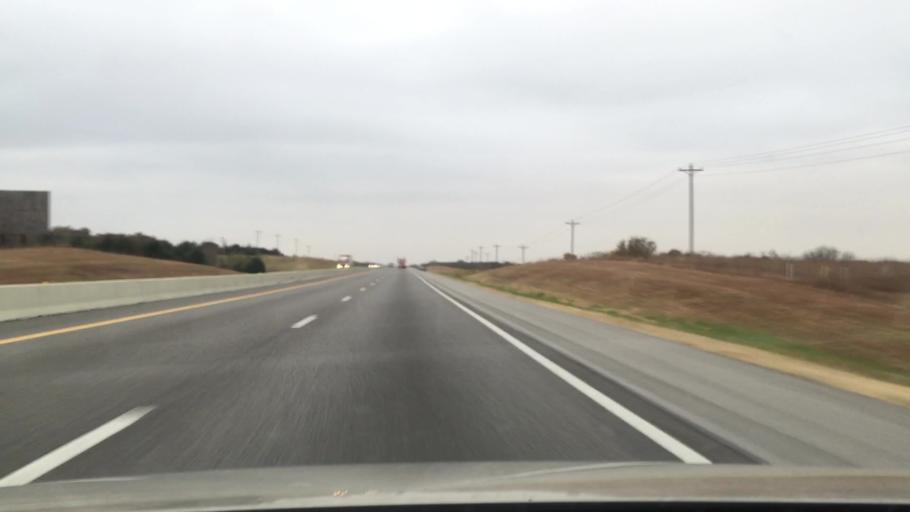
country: US
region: Oklahoma
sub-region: Lincoln County
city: Chandler
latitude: 35.7357
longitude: -96.7933
